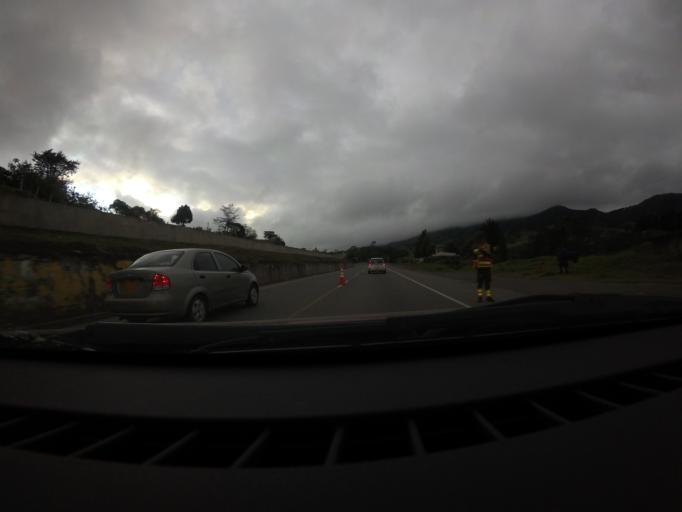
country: CO
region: Boyaca
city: Samaca
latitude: 5.4377
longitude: -73.4457
